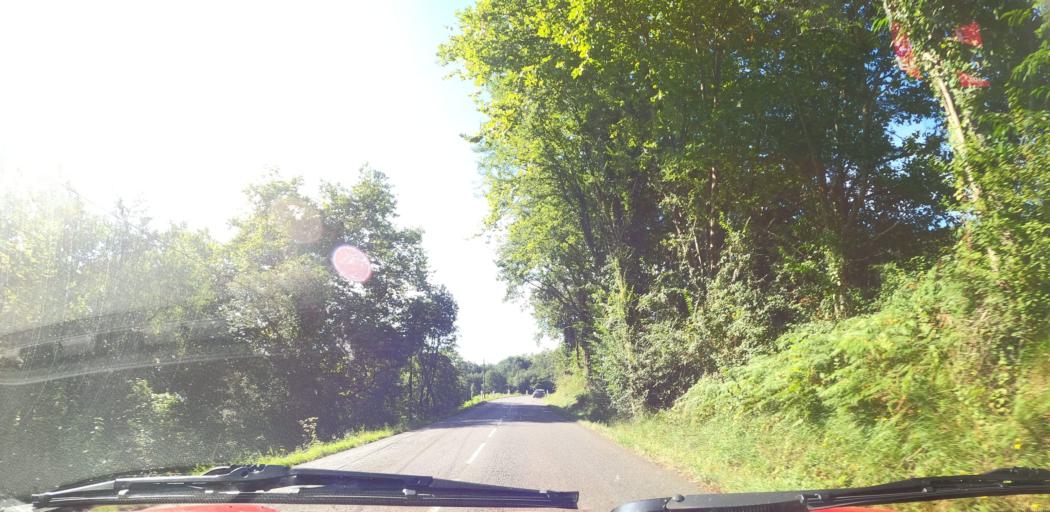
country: FR
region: Aquitaine
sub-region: Departement des Pyrenees-Atlantiques
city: Saint-Pee-sur-Nivelle
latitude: 43.3715
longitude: -1.5456
